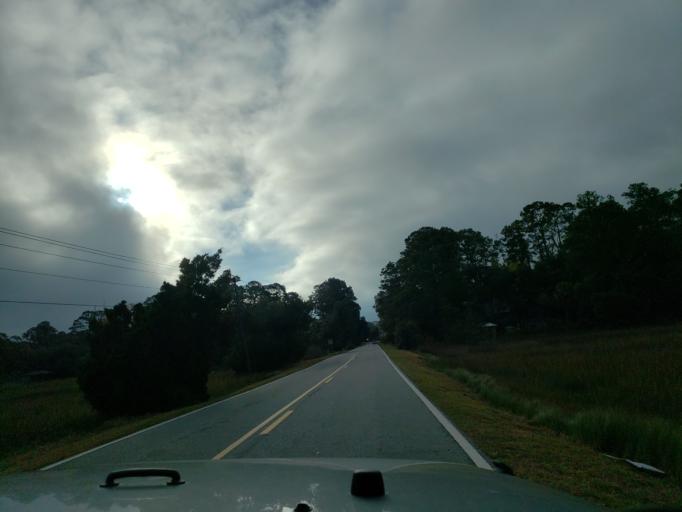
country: US
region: Georgia
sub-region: Chatham County
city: Wilmington Island
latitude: 32.0171
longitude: -80.9617
